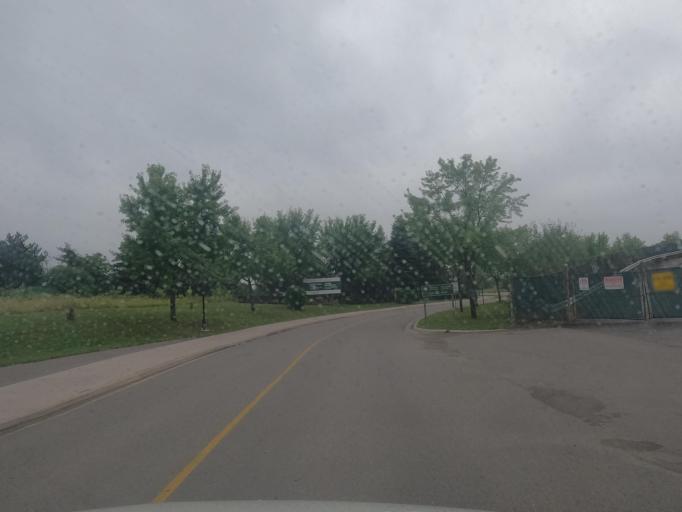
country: CA
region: Ontario
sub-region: Algoma
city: Sault Ste. Marie
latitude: 46.5143
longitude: -84.3473
